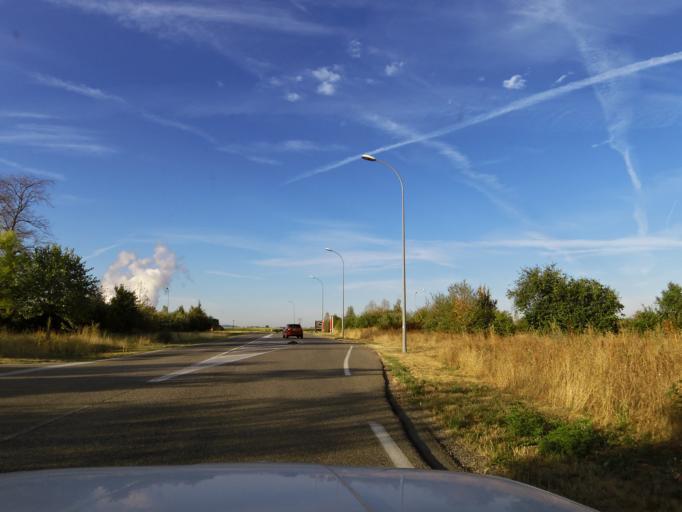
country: FR
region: Rhone-Alpes
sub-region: Departement de l'Isere
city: Hieres-sur-Amby
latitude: 45.8329
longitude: 5.2733
